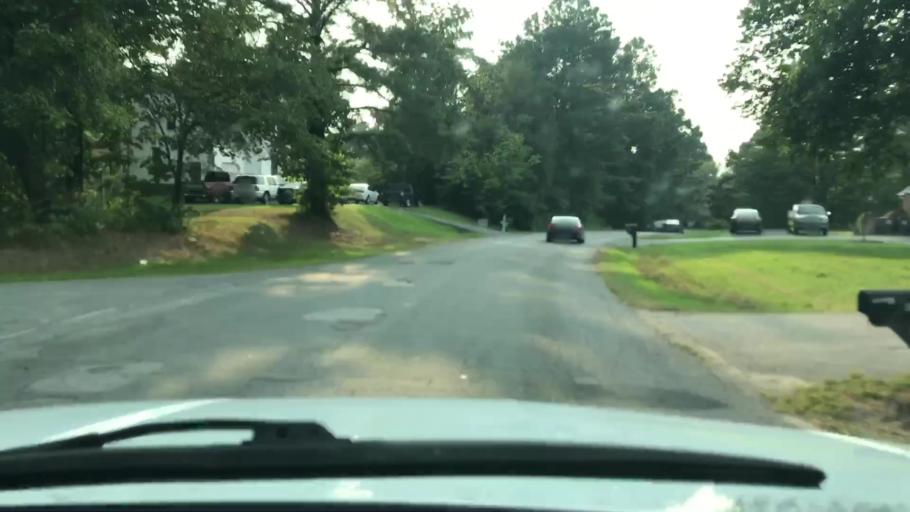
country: US
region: Virginia
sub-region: Chesterfield County
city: Chesterfield
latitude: 37.4438
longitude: -77.5130
